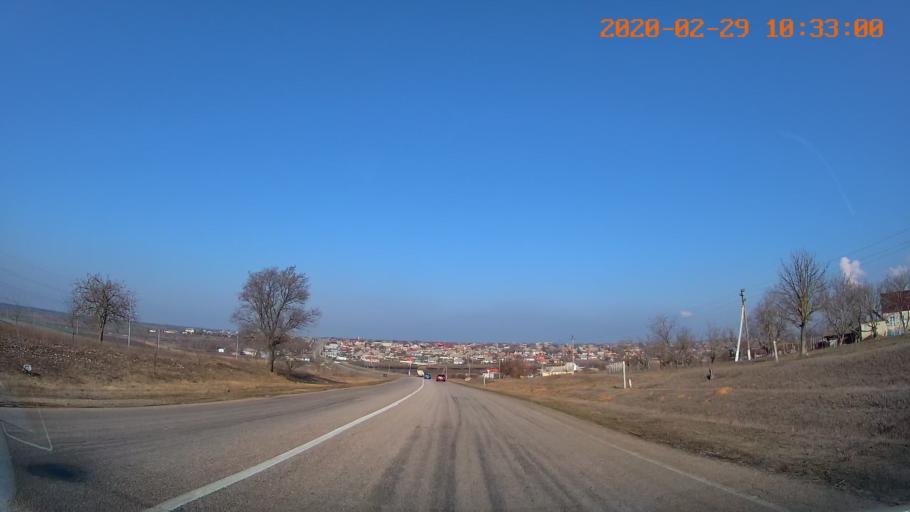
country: UA
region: Odessa
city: Velykoploske
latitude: 46.9673
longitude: 29.5495
